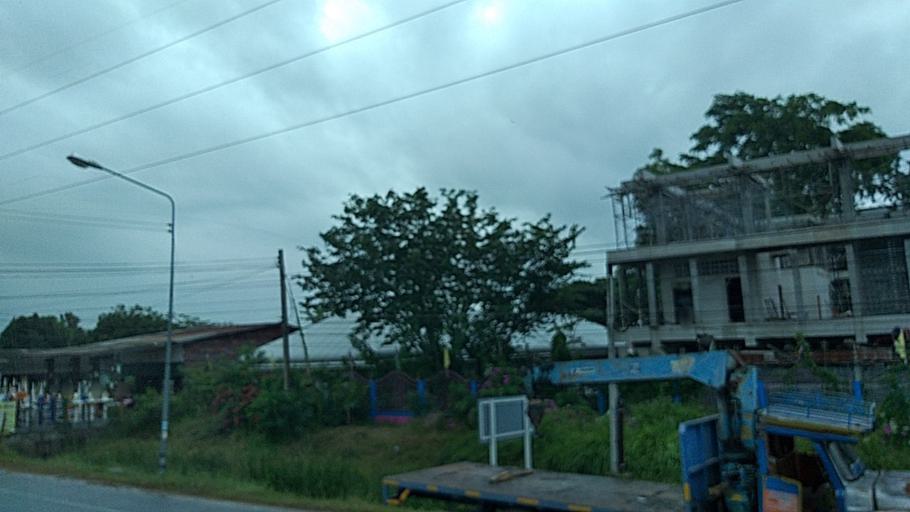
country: TH
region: Maha Sarakham
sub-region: Amphoe Borabue
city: Borabue
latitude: 16.0433
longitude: 103.1254
